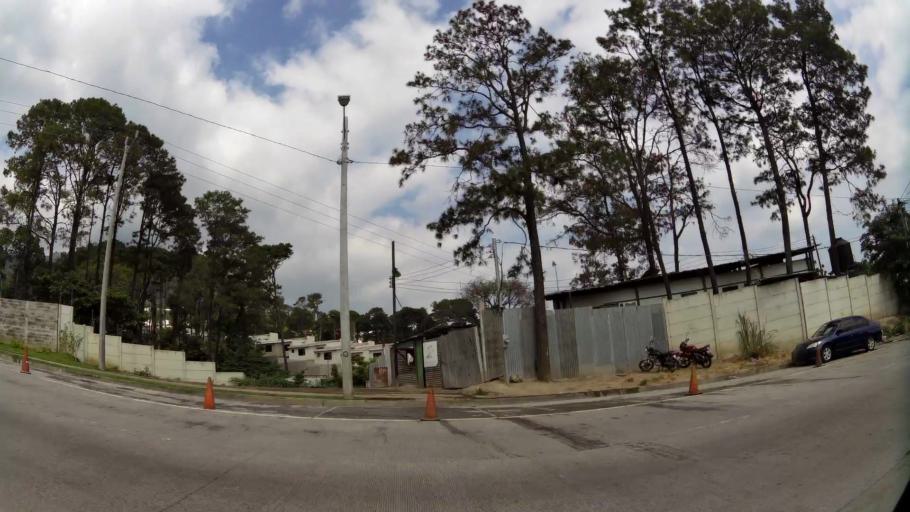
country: SV
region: San Salvador
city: Mejicanos
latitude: 13.7144
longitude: -89.2434
